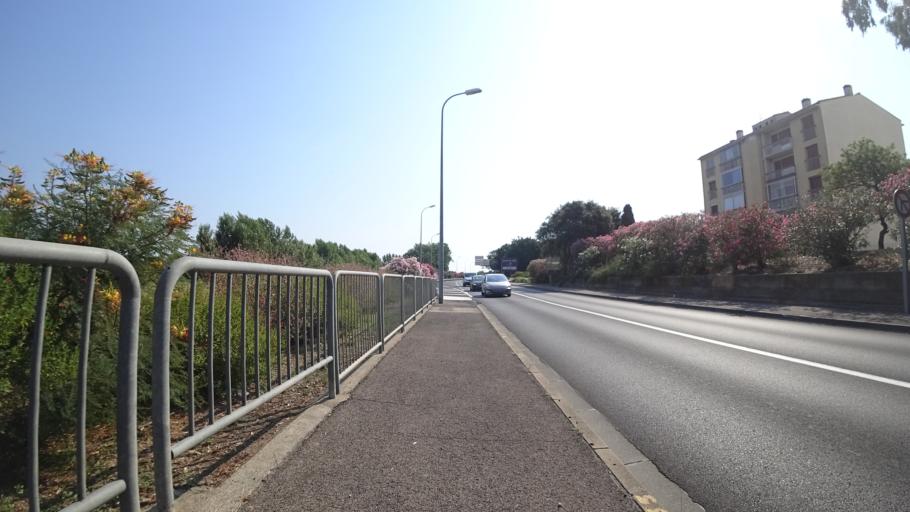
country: FR
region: Languedoc-Roussillon
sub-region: Departement des Pyrenees-Orientales
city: Perpignan
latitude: 42.7065
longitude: 2.9044
